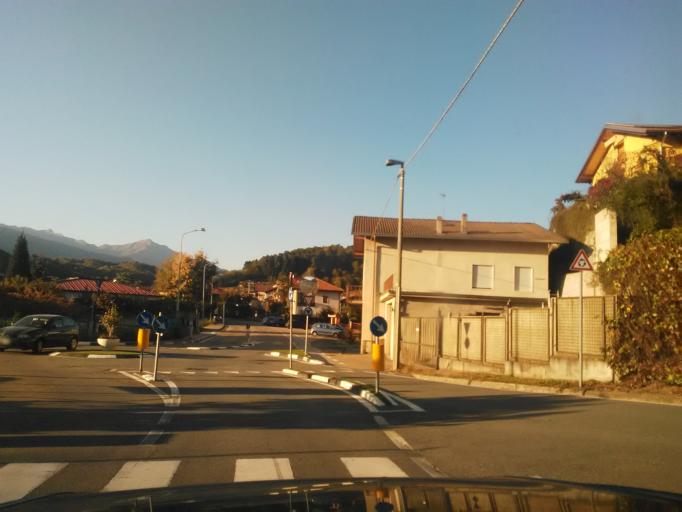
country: IT
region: Piedmont
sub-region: Provincia di Vercelli
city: Borgosesia
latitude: 45.7153
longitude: 8.2878
